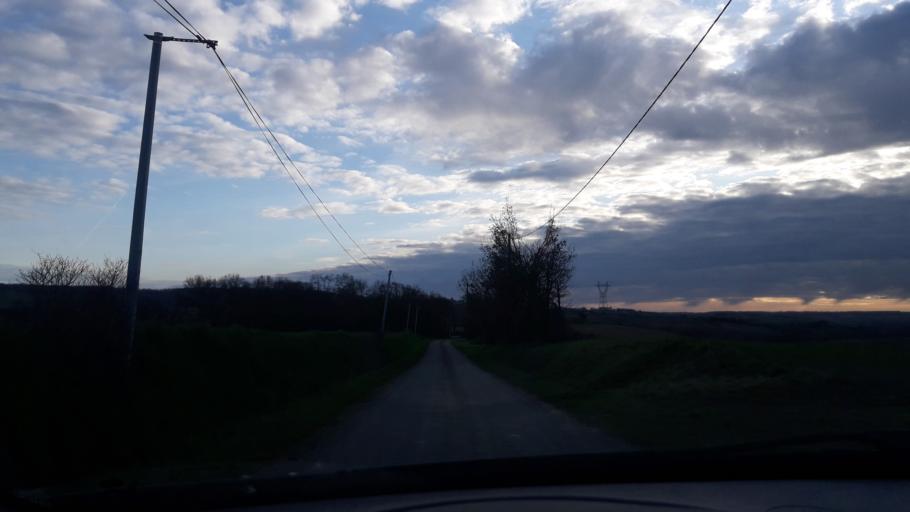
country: FR
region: Midi-Pyrenees
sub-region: Departement du Gers
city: Pujaudran
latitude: 43.6660
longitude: 1.0781
